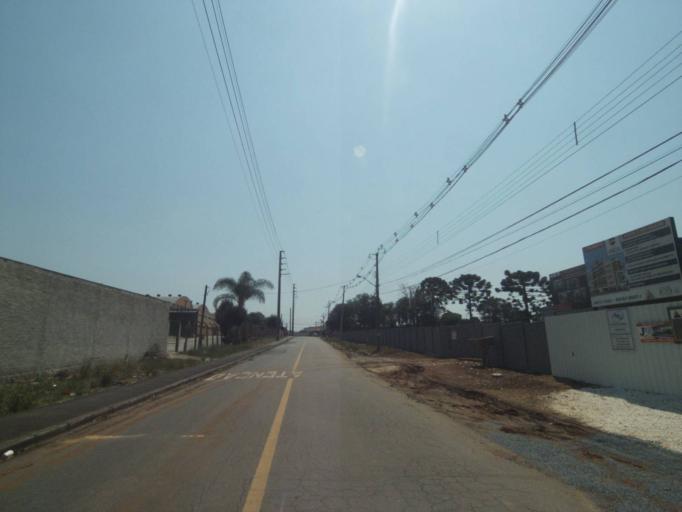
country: BR
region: Parana
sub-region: Sao Jose Dos Pinhais
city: Sao Jose dos Pinhais
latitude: -25.4985
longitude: -49.2704
